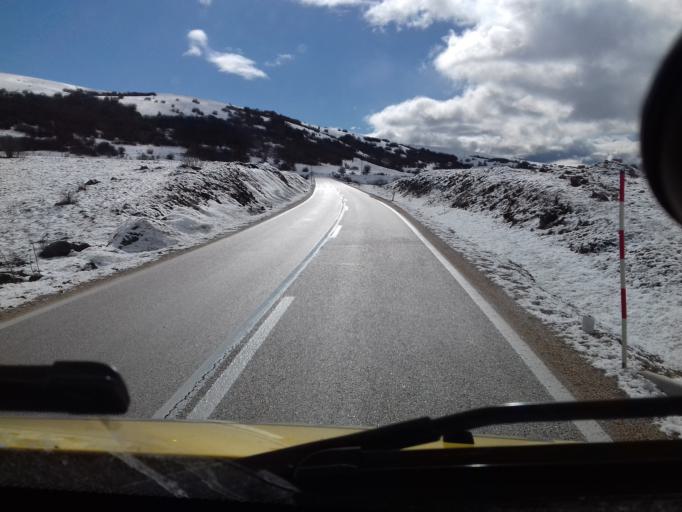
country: BA
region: Federation of Bosnia and Herzegovina
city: Tomislavgrad
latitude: 43.8149
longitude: 17.2001
